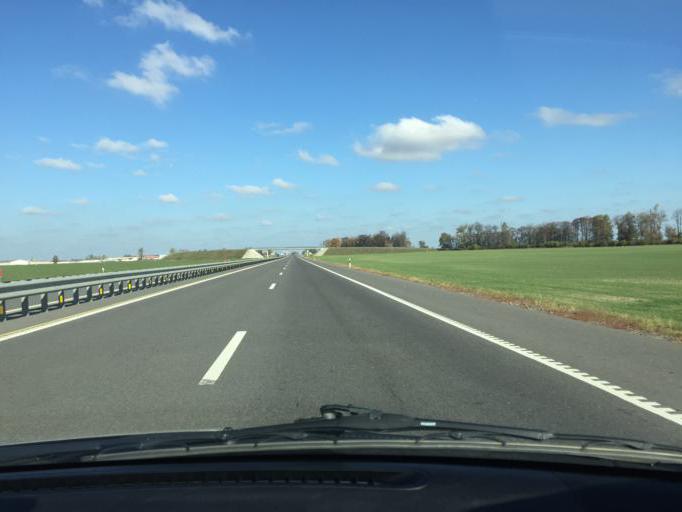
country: BY
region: Minsk
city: Slutsk
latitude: 53.0629
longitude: 27.5480
